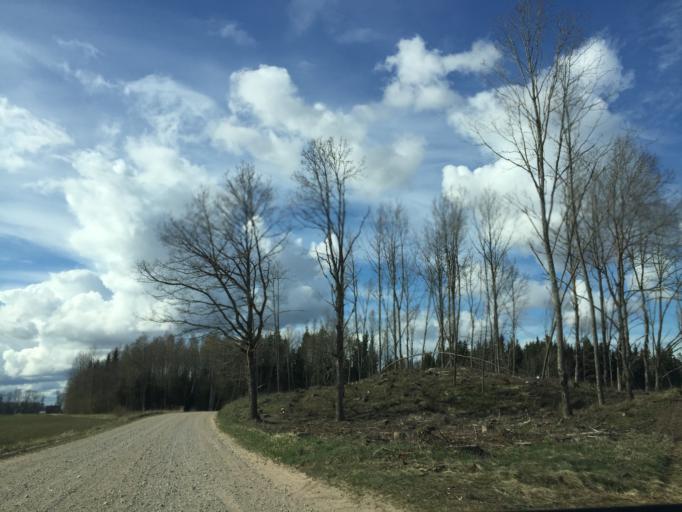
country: LV
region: Burtnieki
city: Matisi
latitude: 57.6072
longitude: 25.0431
